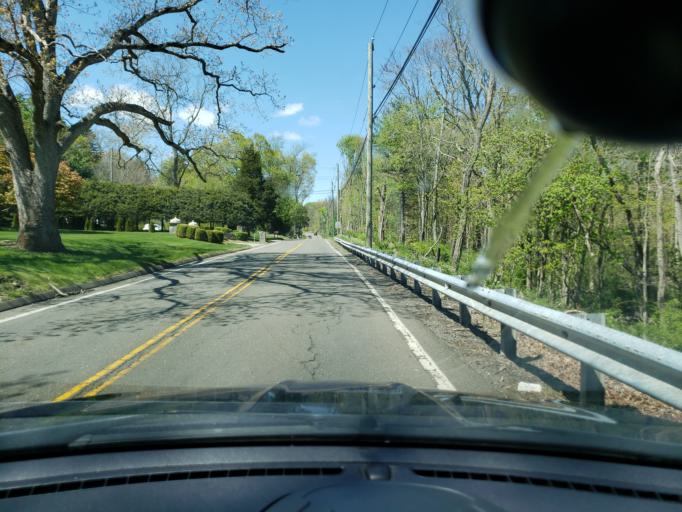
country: US
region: Connecticut
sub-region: New Haven County
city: Orange
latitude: 41.3046
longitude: -73.0188
